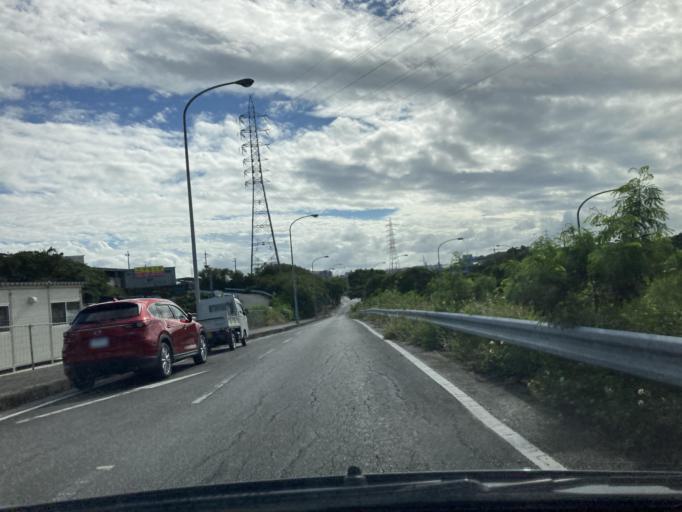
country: JP
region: Okinawa
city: Tomigusuku
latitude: 26.1729
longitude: 127.7273
